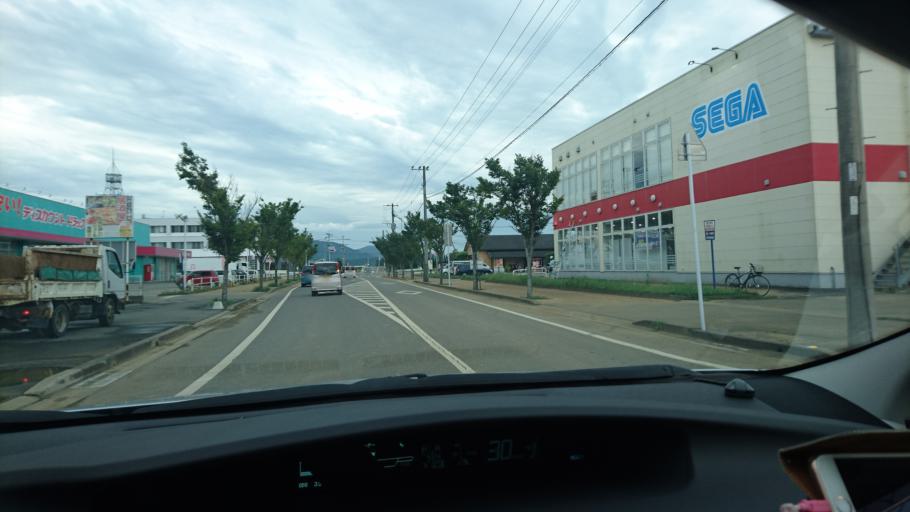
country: JP
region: Saga Prefecture
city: Takeocho-takeo
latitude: 33.1997
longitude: 130.0347
